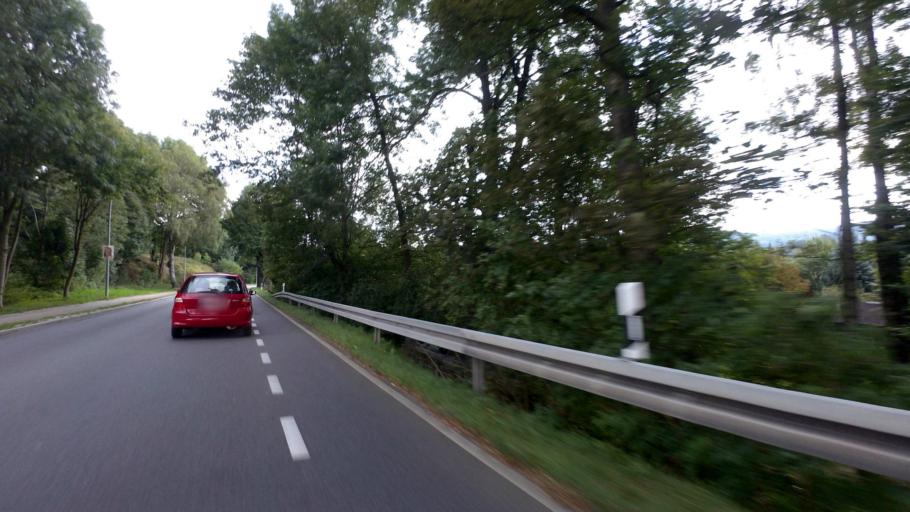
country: DE
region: Saxony
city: Crostau
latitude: 51.1003
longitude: 14.4658
